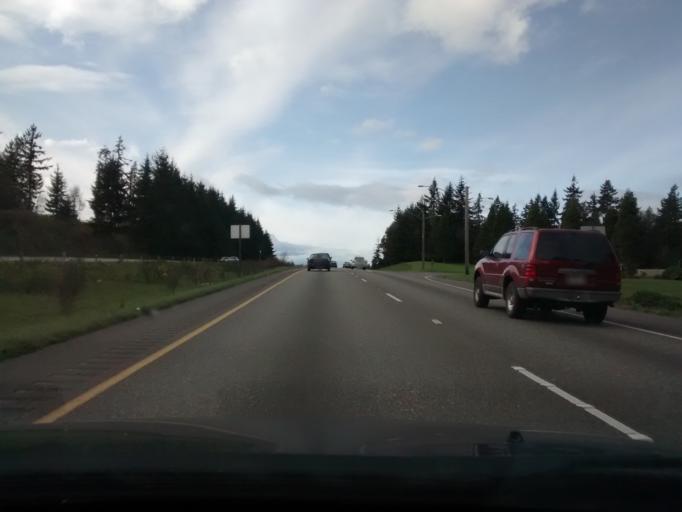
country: US
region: Washington
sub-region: Pierce County
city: Gig Harbor
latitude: 47.3335
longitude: -122.6017
